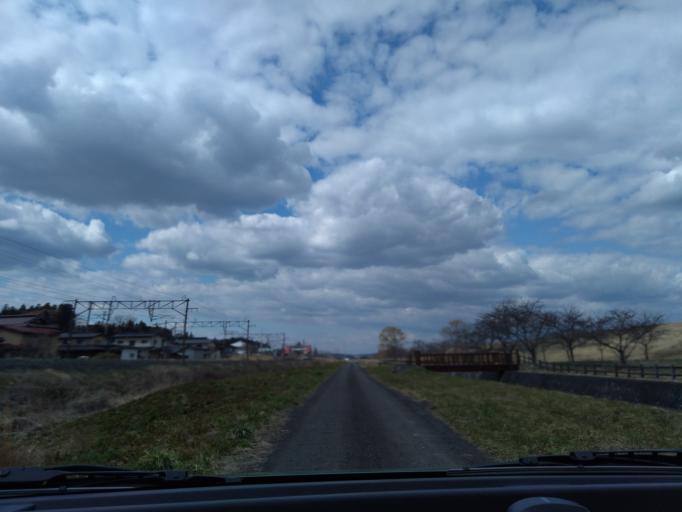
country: JP
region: Iwate
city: Ichinoseki
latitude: 38.9487
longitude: 141.1334
